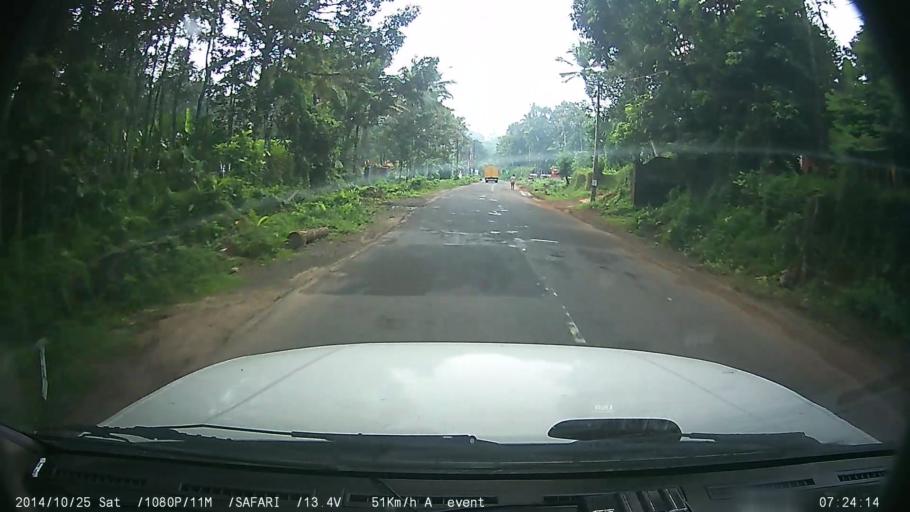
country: IN
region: Kerala
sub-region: Kottayam
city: Palackattumala
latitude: 9.7877
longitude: 76.5793
